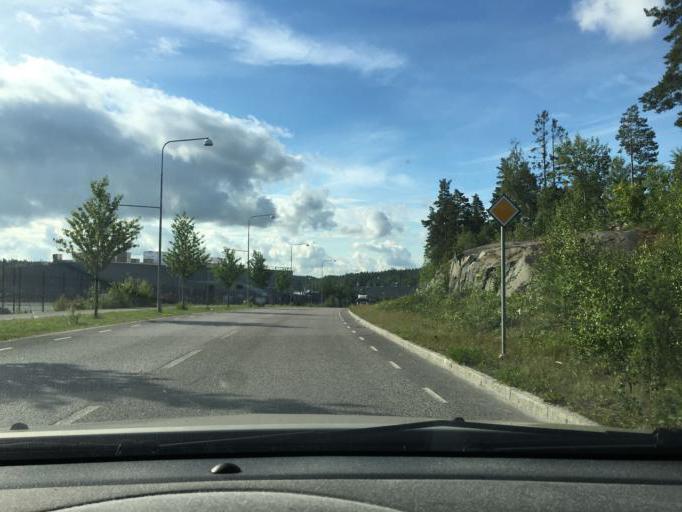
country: SE
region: Stockholm
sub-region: Sodertalje Kommun
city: Soedertaelje
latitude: 59.2059
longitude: 17.6637
